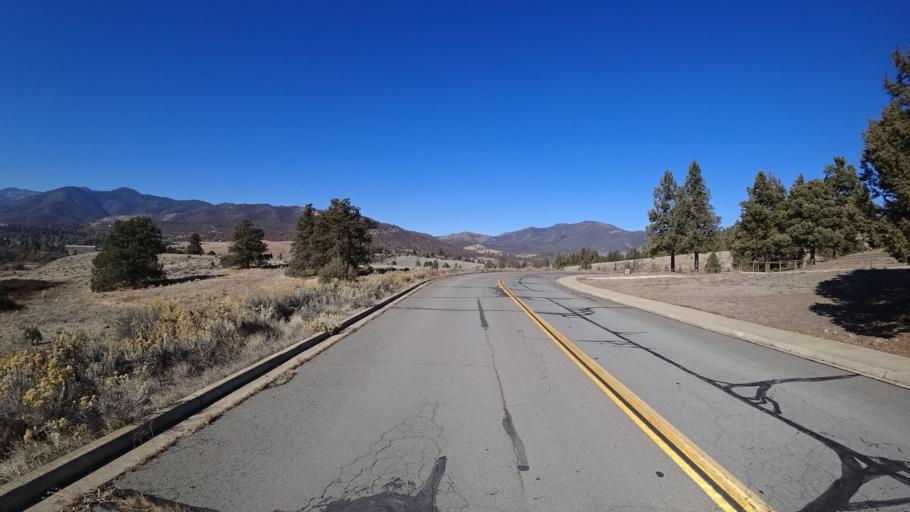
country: US
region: California
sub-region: Siskiyou County
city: Yreka
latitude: 41.7392
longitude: -122.6211
